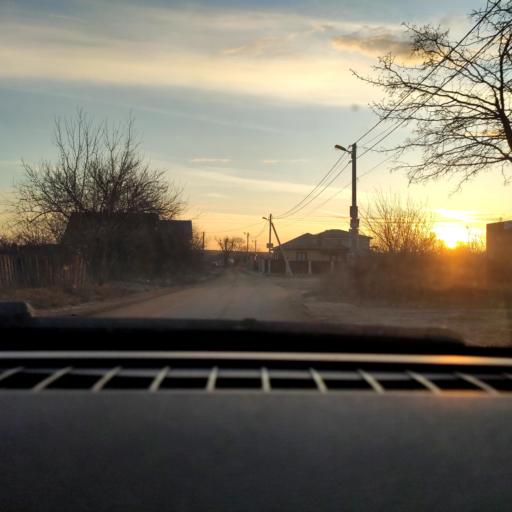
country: RU
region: Voronezj
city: Maslovka
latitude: 51.6148
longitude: 39.2670
